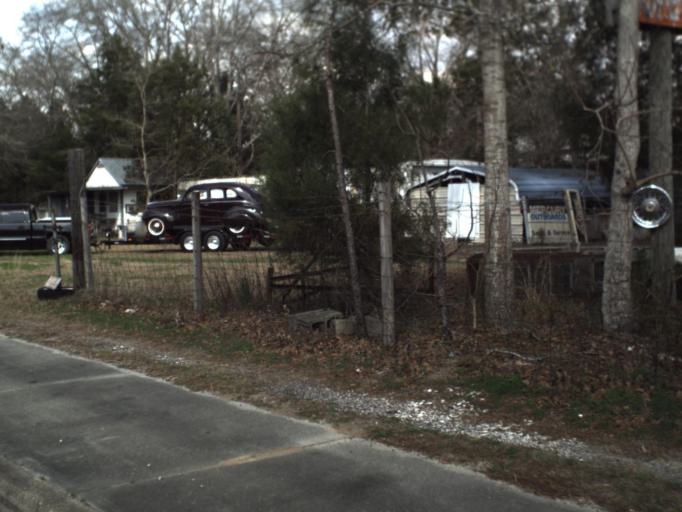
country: US
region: Florida
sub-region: Bay County
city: Youngstown
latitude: 30.3725
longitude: -85.4383
